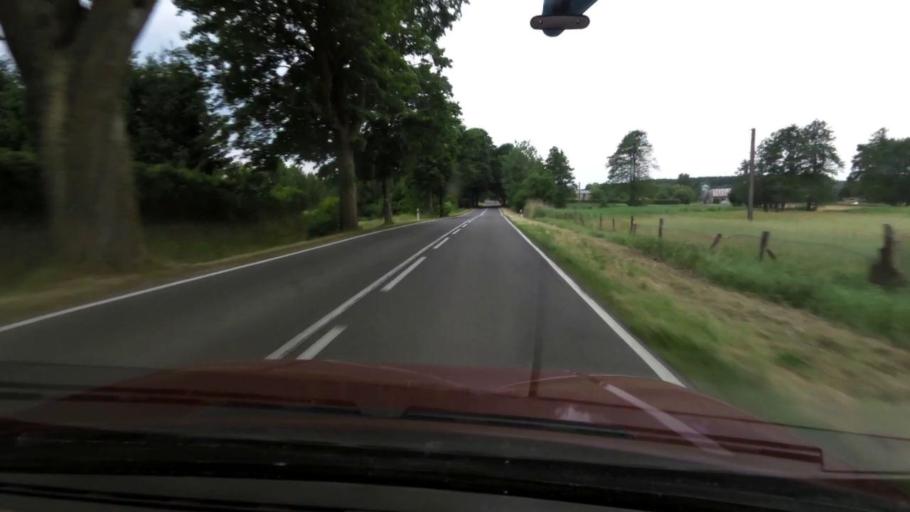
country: PL
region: West Pomeranian Voivodeship
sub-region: Powiat koszalinski
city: Sianow
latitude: 54.1828
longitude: 16.3211
